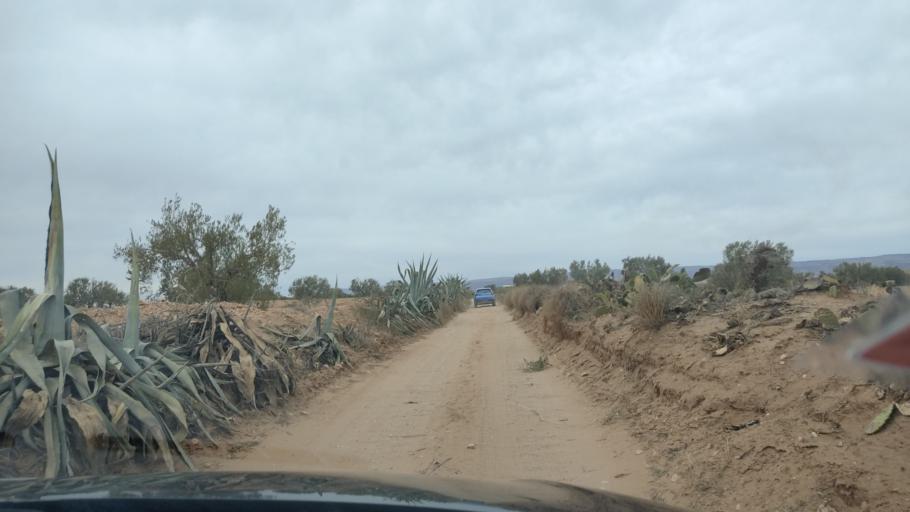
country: TN
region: Al Qasrayn
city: Kasserine
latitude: 35.2239
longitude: 8.9380
